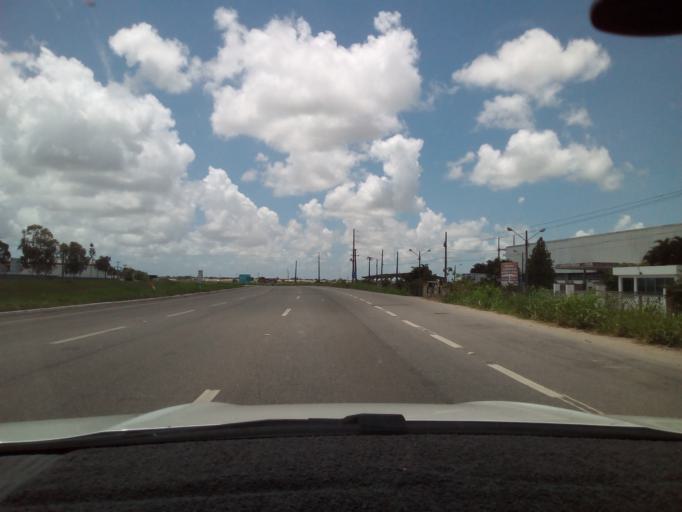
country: BR
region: Paraiba
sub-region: Santa Rita
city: Santa Rita
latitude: -7.1429
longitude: -34.9905
